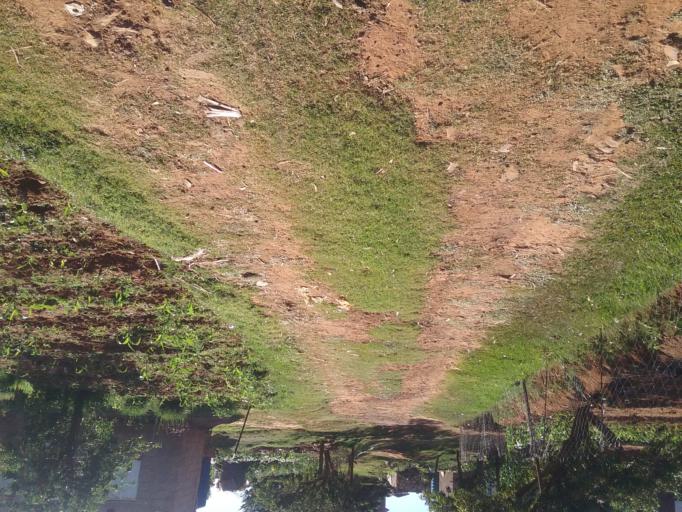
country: LS
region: Maseru
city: Maseru
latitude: -29.4234
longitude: 27.5692
